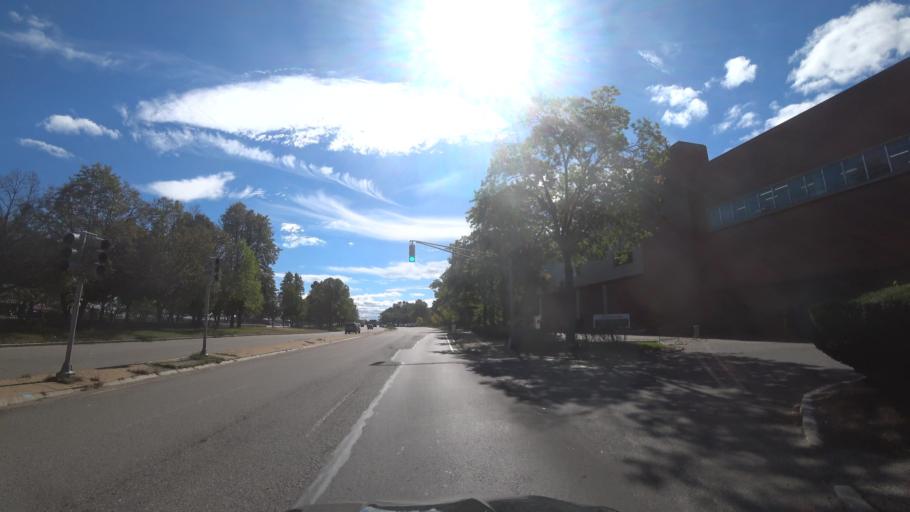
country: US
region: Massachusetts
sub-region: Suffolk County
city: South Boston
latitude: 42.3160
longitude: -71.0485
